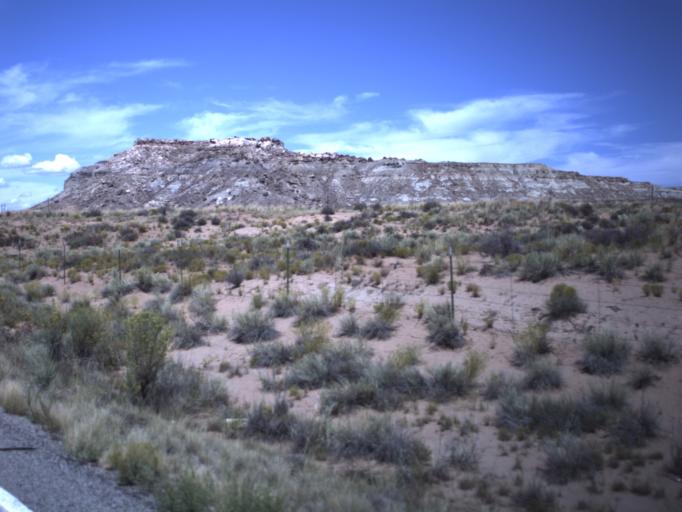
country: US
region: Utah
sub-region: San Juan County
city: Blanding
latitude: 37.2936
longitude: -109.4222
